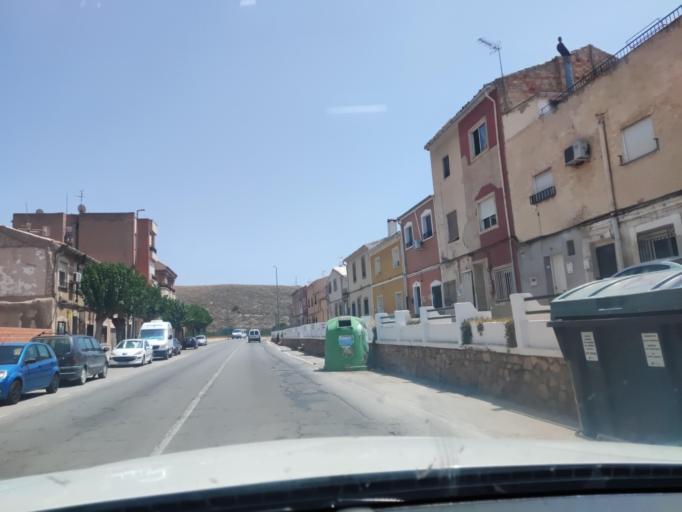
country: ES
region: Castille-La Mancha
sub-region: Provincia de Albacete
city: Hellin
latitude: 38.5161
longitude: -1.6983
